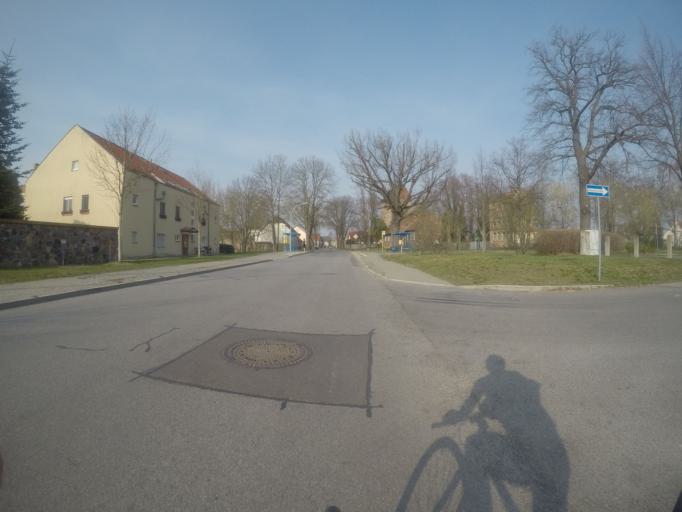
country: DE
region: Brandenburg
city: Schonefeld
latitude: 52.3574
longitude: 13.4718
